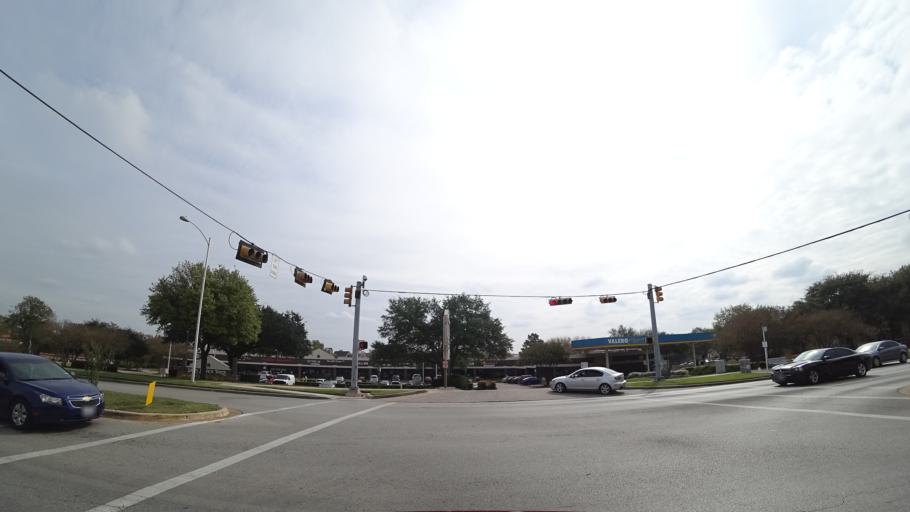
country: US
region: Texas
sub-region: Travis County
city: Wells Branch
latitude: 30.4360
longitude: -97.6749
